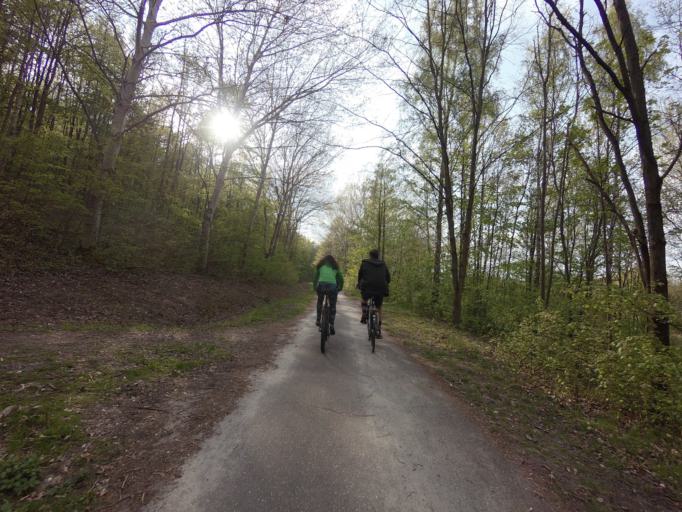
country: NL
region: Limburg
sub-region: Gemeente Heerlen
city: Nieuw-Lotbroek
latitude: 50.9166
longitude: 5.9448
